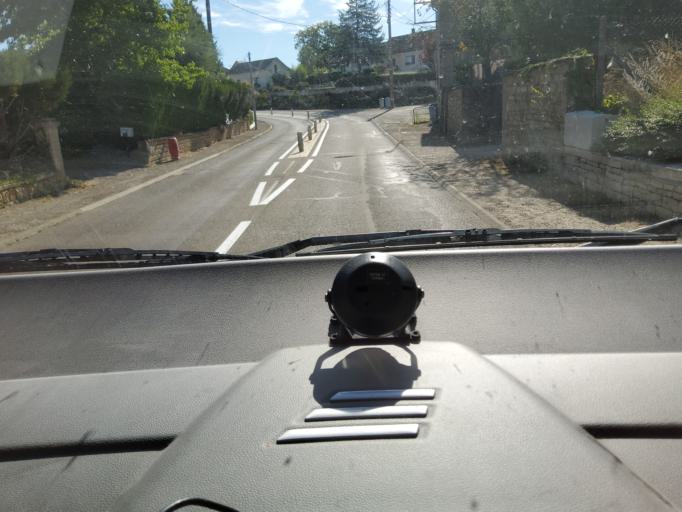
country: FR
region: Franche-Comte
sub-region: Departement du Jura
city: Champvans
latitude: 47.1051
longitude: 5.4392
